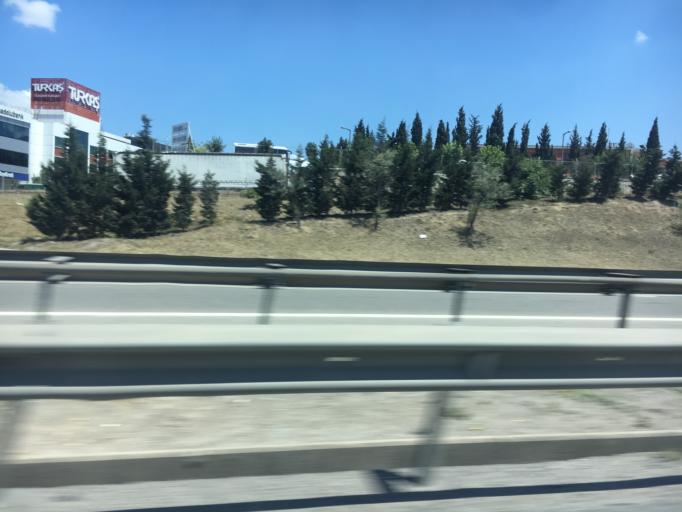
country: TR
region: Kocaeli
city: Balcik
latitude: 40.8797
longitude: 29.3827
